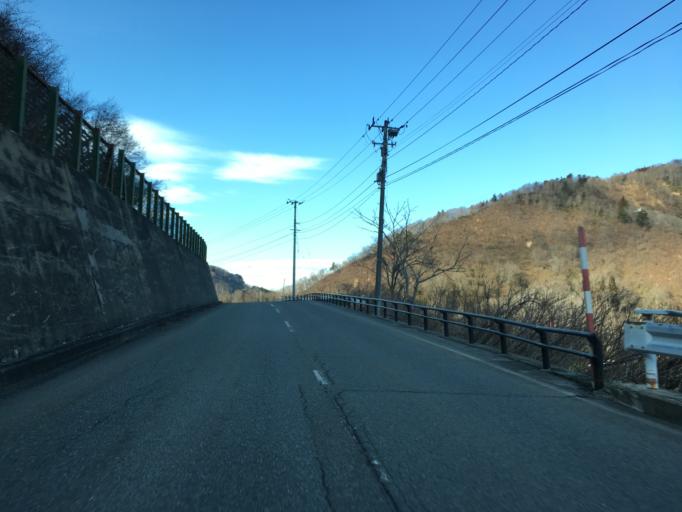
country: JP
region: Yamagata
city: Nagai
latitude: 37.9583
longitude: 139.9171
